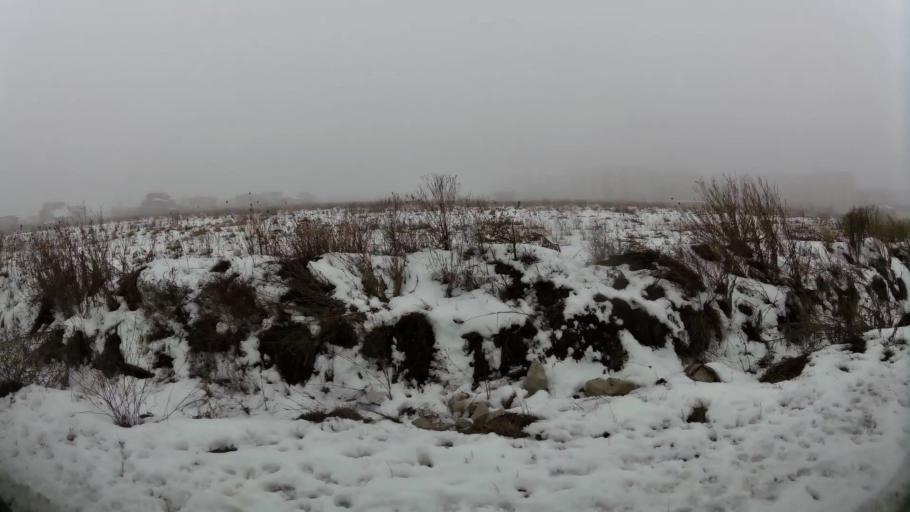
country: RO
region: Ilfov
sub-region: Comuna Chiajna
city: Rosu
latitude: 44.4409
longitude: 25.9933
